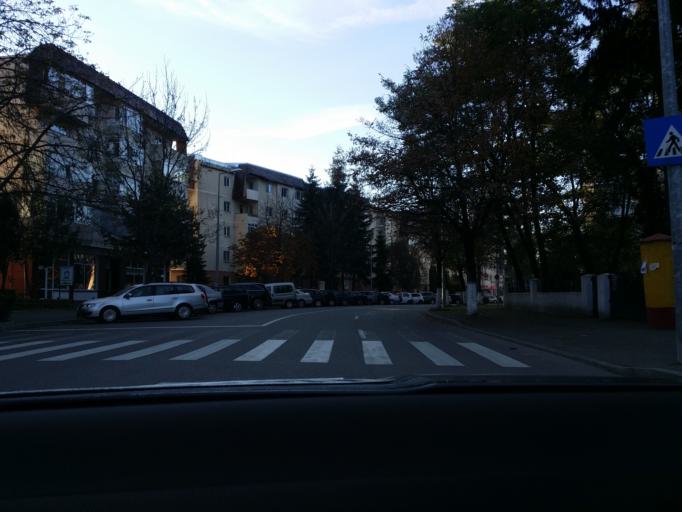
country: RO
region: Prahova
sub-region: Municipiul Campina
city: Campina
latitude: 45.1310
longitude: 25.7341
